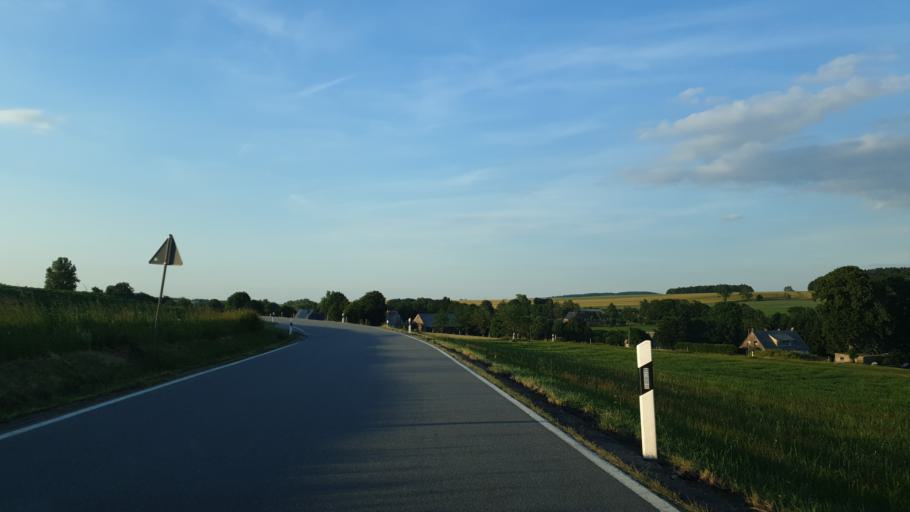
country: DE
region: Saxony
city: Lossnitz
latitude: 50.6704
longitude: 12.7351
